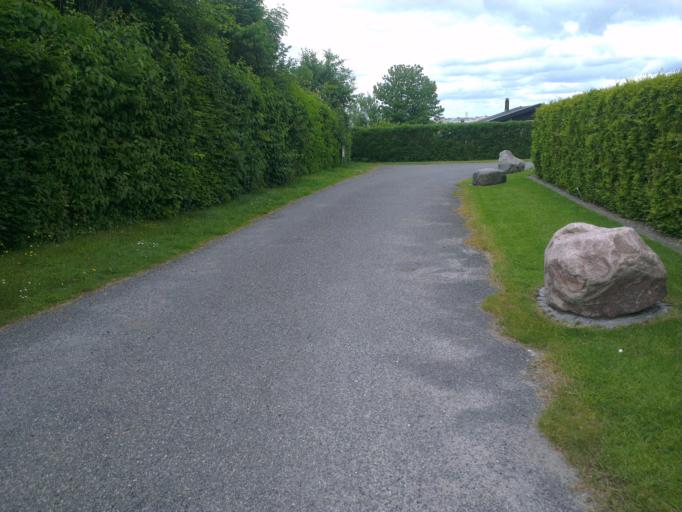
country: DK
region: Capital Region
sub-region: Frederikssund Kommune
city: Frederikssund
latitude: 55.8114
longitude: 12.0385
